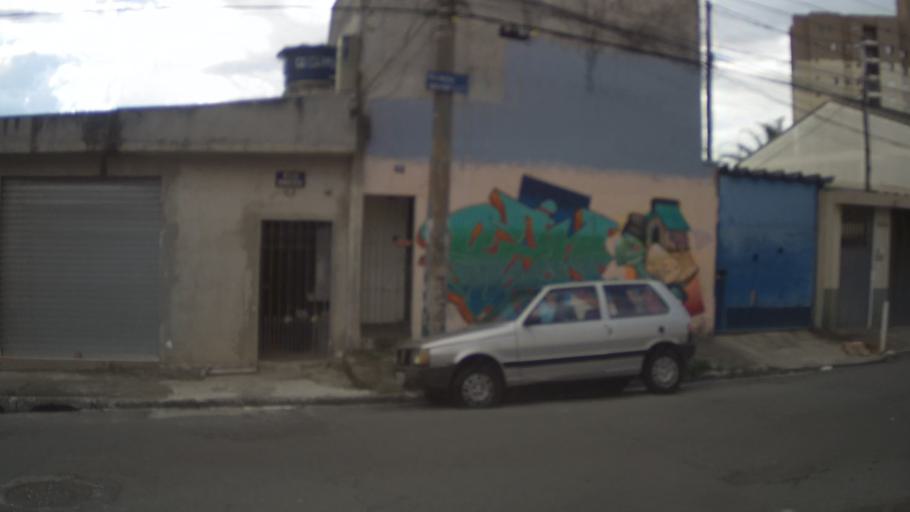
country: BR
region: Sao Paulo
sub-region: Guarulhos
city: Guarulhos
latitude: -23.4800
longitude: -46.5541
